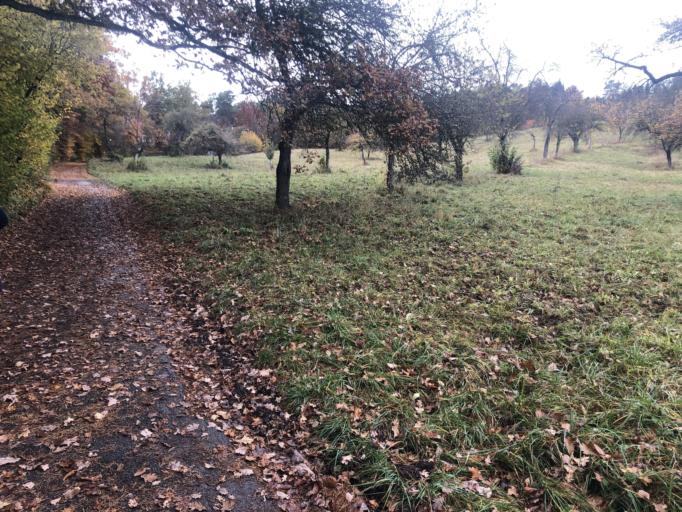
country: DE
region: Baden-Wuerttemberg
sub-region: Tuebingen Region
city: Tuebingen
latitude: 48.5284
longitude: 9.0290
